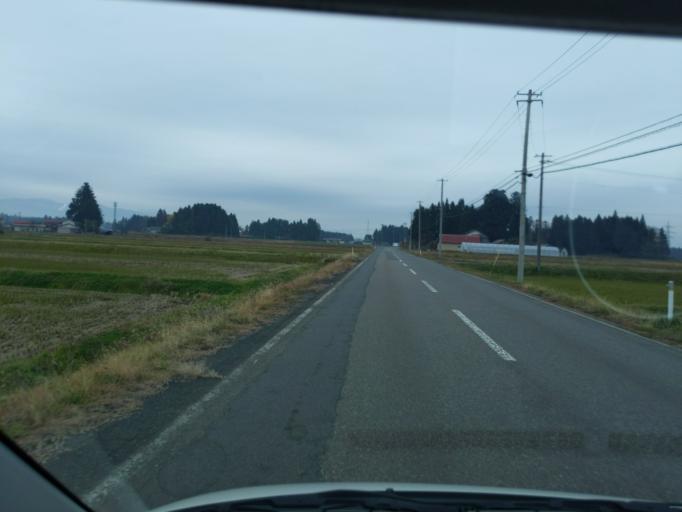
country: JP
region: Iwate
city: Mizusawa
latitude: 39.0966
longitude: 141.0964
